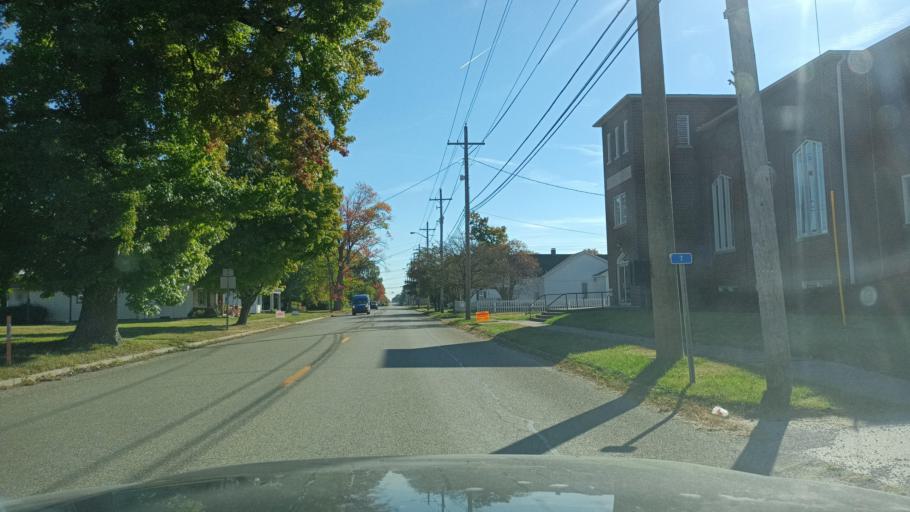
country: US
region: Indiana
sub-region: Vigo County
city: Seelyville
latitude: 39.3903
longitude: -87.3010
